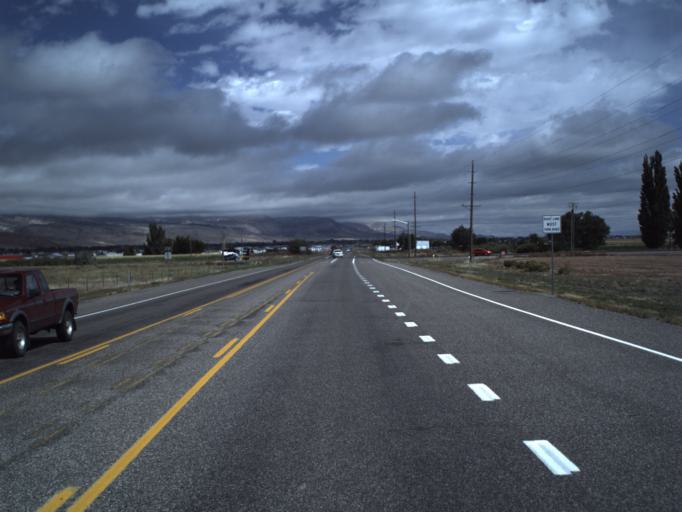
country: US
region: Utah
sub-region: Sevier County
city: Richfield
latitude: 38.7224
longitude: -112.1009
